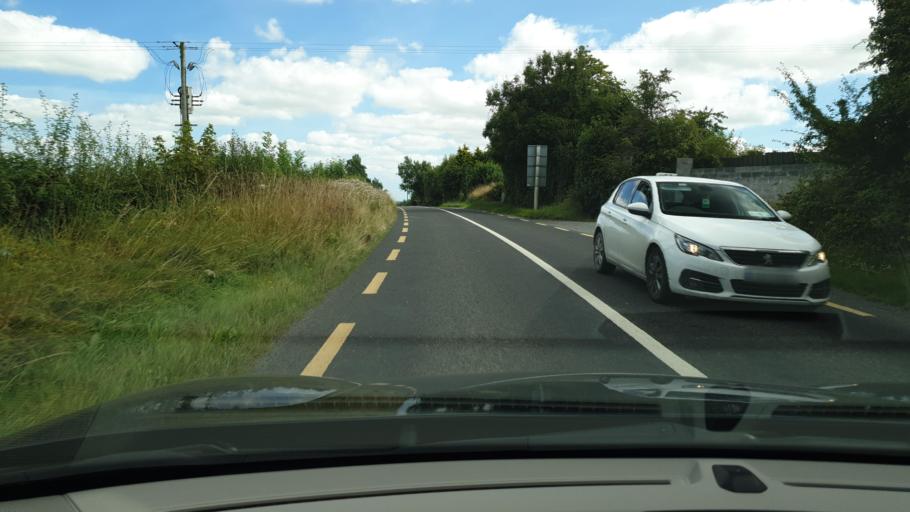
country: IE
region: Leinster
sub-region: Kildare
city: Kilcock
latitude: 53.4572
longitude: -6.6334
